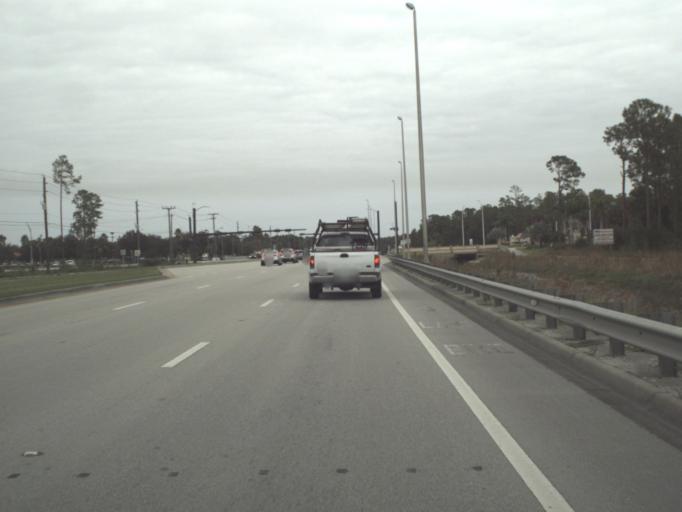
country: US
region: Florida
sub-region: Collier County
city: Lely Resort
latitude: 26.1074
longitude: -81.6870
